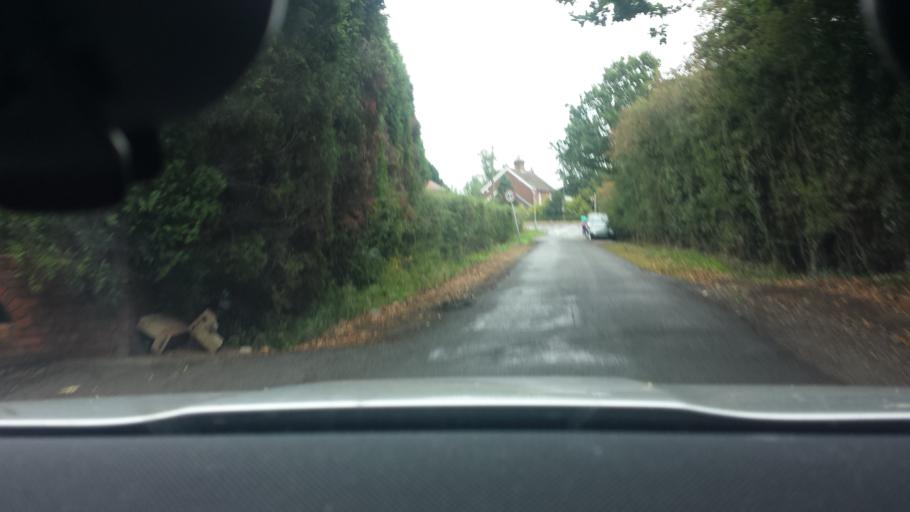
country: GB
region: England
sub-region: Kent
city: Staplehurst
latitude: 51.1727
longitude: 0.5514
